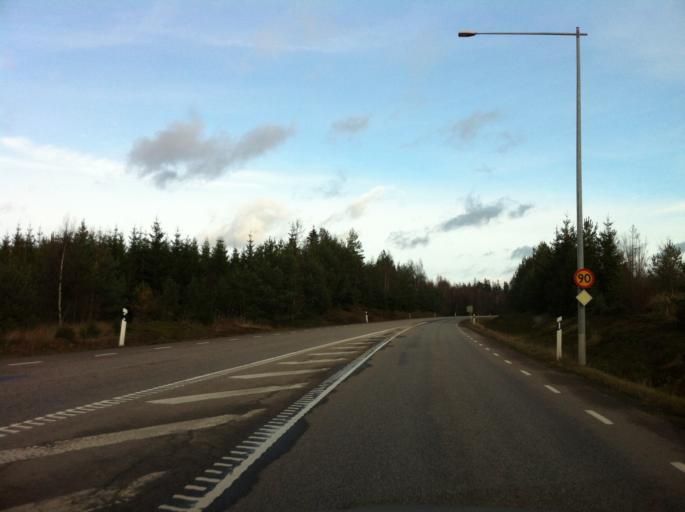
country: SE
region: Kronoberg
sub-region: Almhults Kommun
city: AElmhult
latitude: 56.5688
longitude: 14.1839
